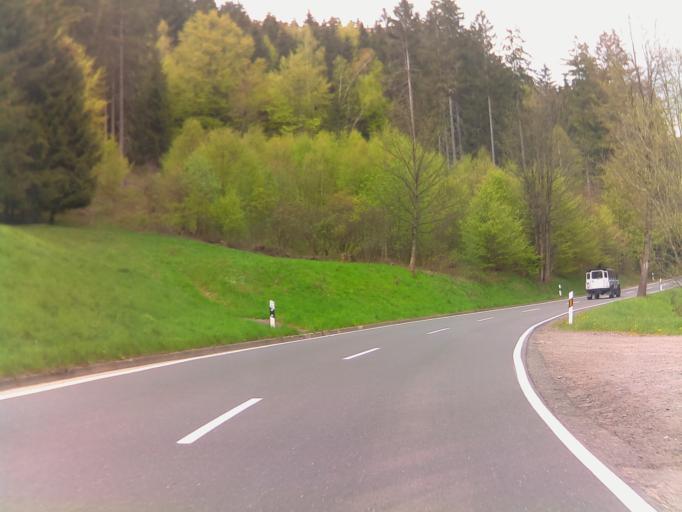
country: DE
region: Bavaria
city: Foritz
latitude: 50.3615
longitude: 11.2244
